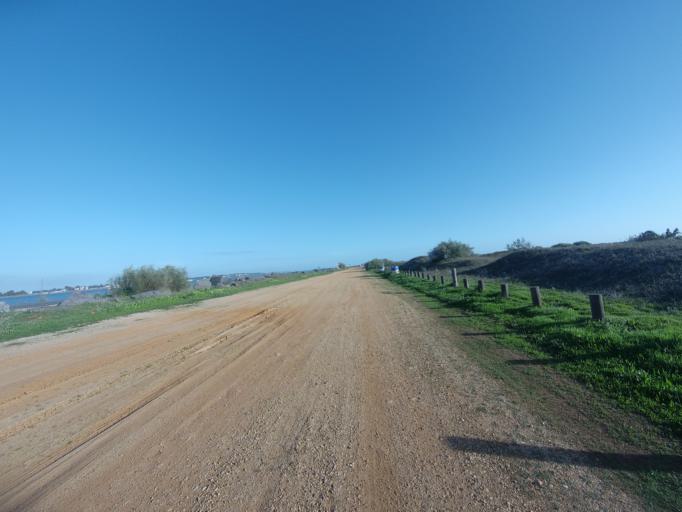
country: ES
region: Andalusia
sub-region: Provincia de Huelva
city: Punta Umbria
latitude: 37.1494
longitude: -6.8955
